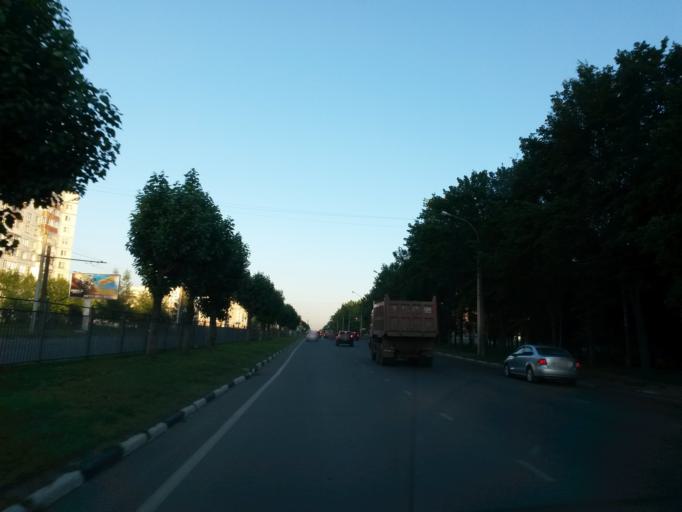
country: RU
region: Jaroslavl
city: Yaroslavl
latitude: 57.6921
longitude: 39.7737
